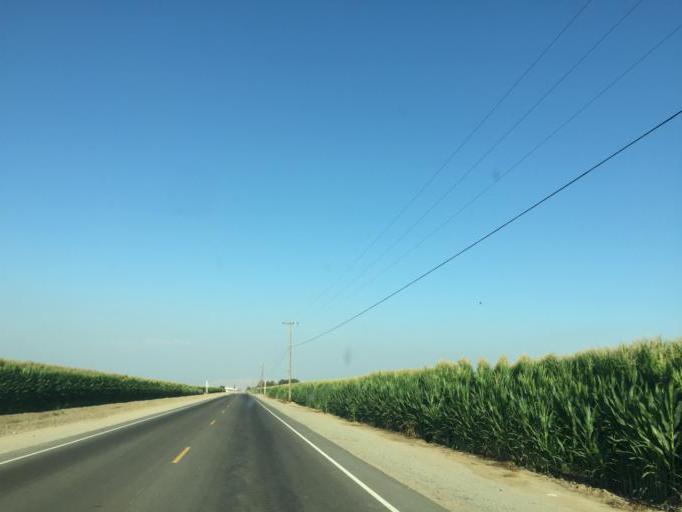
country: US
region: California
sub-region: Tulare County
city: London
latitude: 36.4582
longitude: -119.3614
